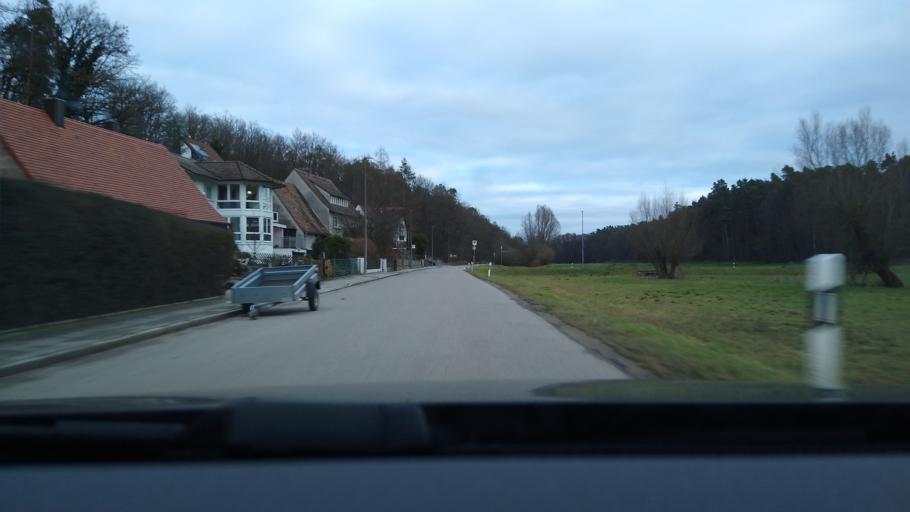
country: DE
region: Bavaria
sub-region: Regierungsbezirk Mittelfranken
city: Schwabach
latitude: 49.3667
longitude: 11.0033
